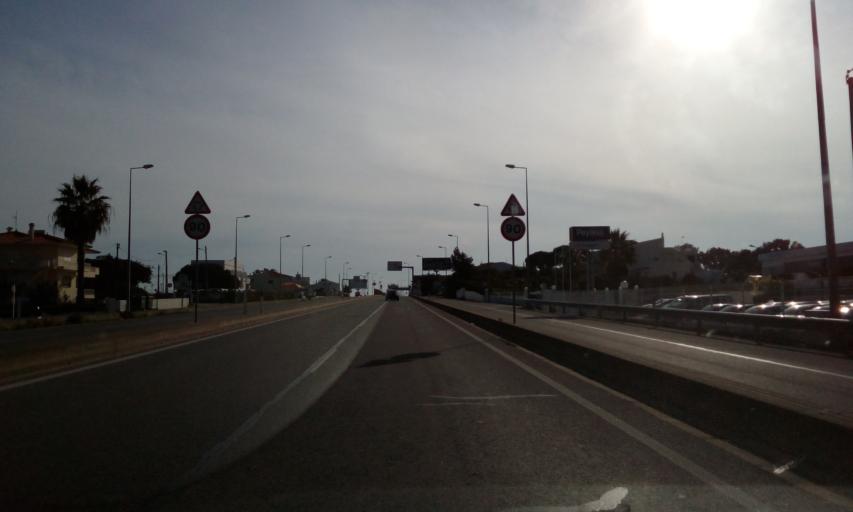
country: PT
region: Faro
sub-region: Faro
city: Faro
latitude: 37.0266
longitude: -7.9695
